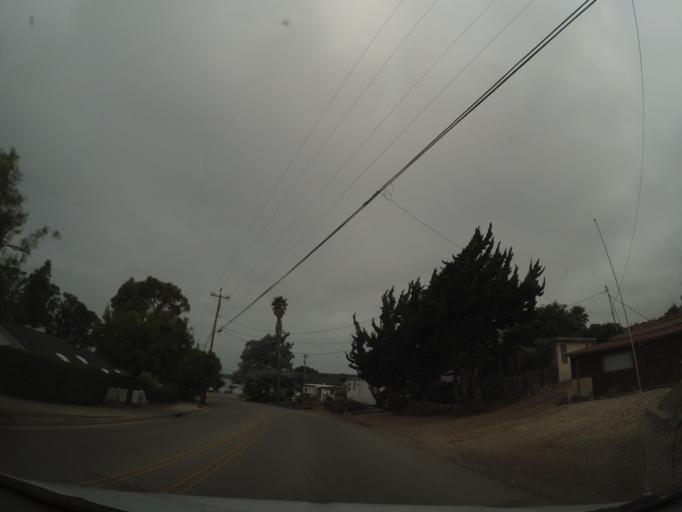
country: US
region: California
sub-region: San Luis Obispo County
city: Morro Bay
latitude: 35.3559
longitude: -120.8449
